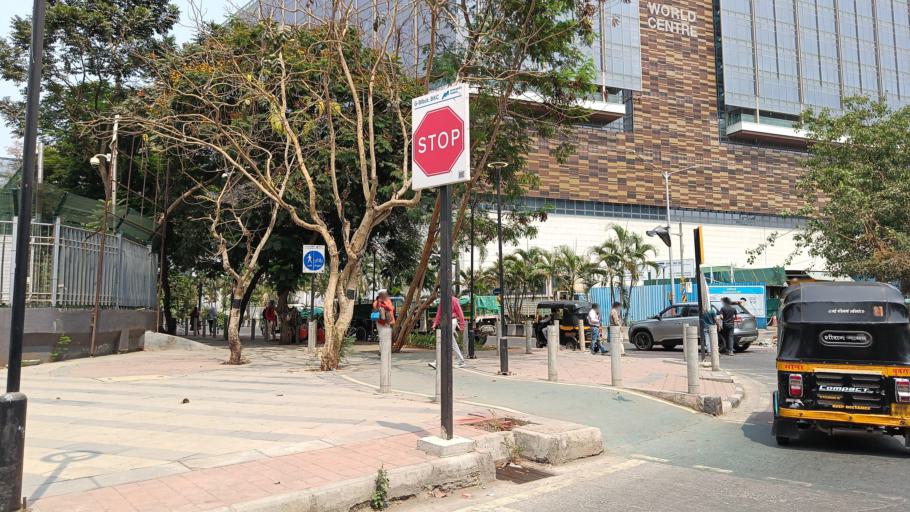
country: IN
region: Maharashtra
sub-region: Mumbai Suburban
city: Mumbai
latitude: 19.0630
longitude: 72.8649
